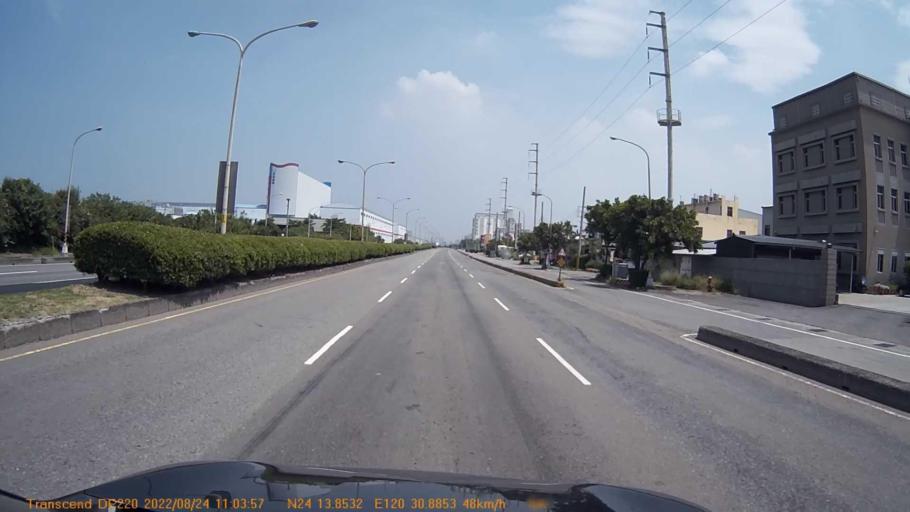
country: TW
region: Taiwan
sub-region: Changhua
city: Chang-hua
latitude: 24.2314
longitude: 120.5150
